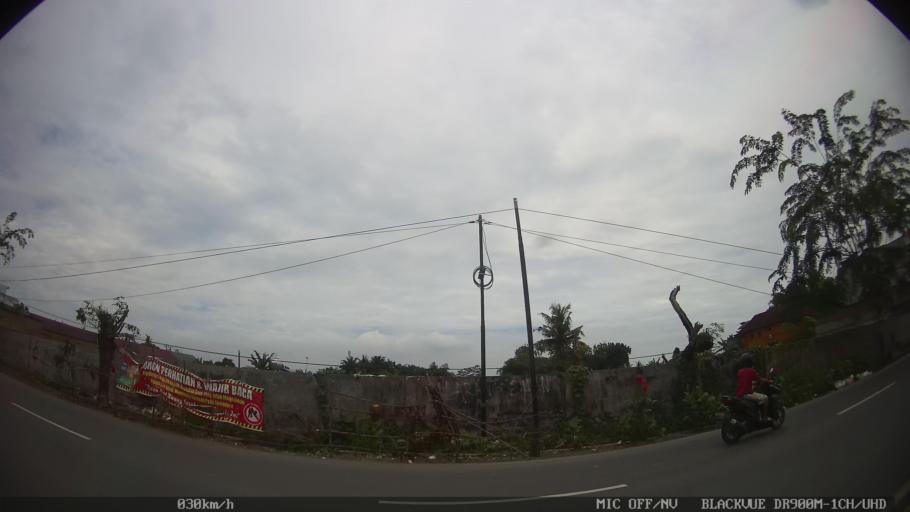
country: ID
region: North Sumatra
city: Sunggal
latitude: 3.5996
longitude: 98.5599
